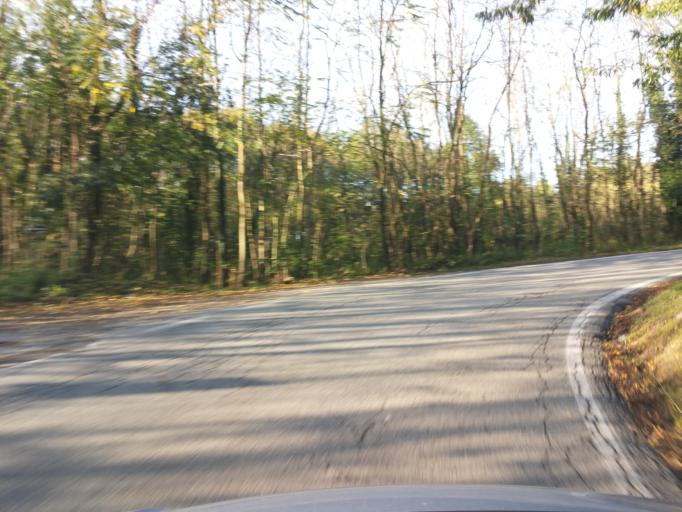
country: IT
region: Piedmont
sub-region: Provincia di Torino
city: Mazze
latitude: 45.2988
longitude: 7.9456
